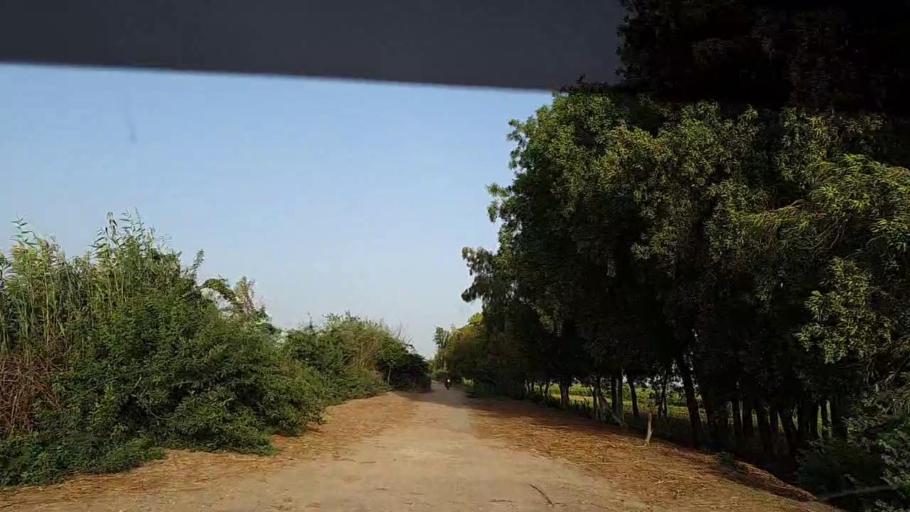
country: PK
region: Sindh
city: Kadhan
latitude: 24.5470
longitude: 68.9261
